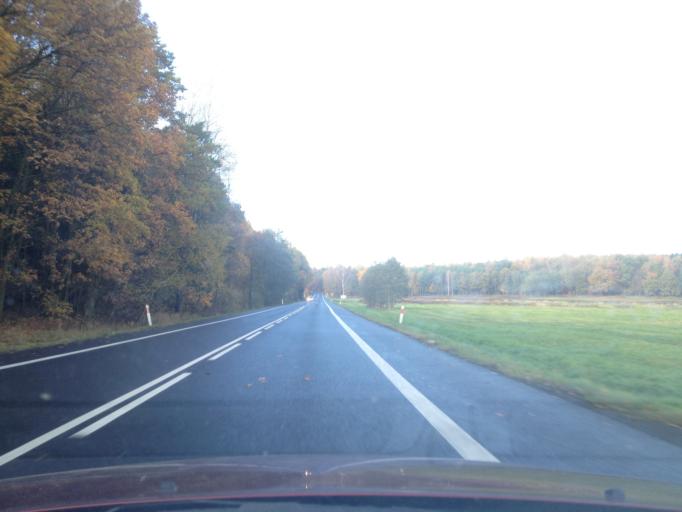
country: PL
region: Lower Silesian Voivodeship
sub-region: Powiat zgorzelecki
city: Lagow
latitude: 51.1542
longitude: 15.0712
